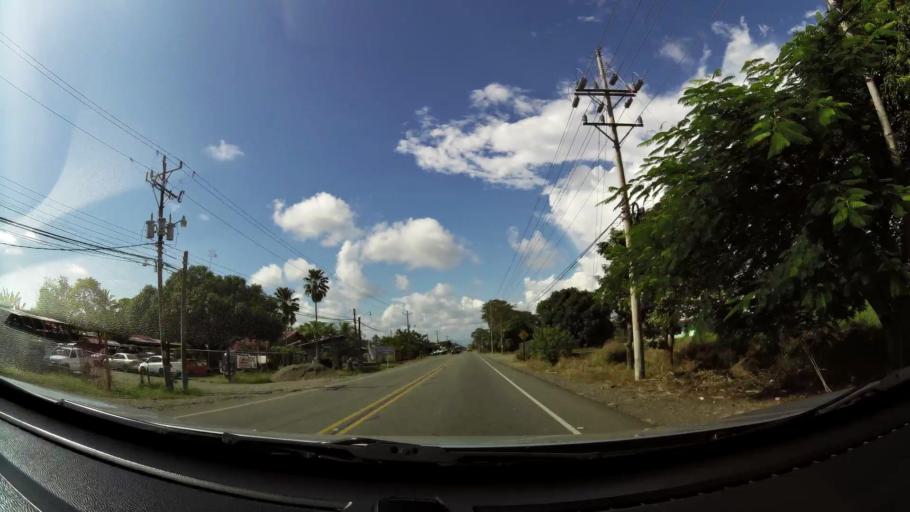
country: CR
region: Puntarenas
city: Quepos
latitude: 9.4616
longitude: -84.1822
